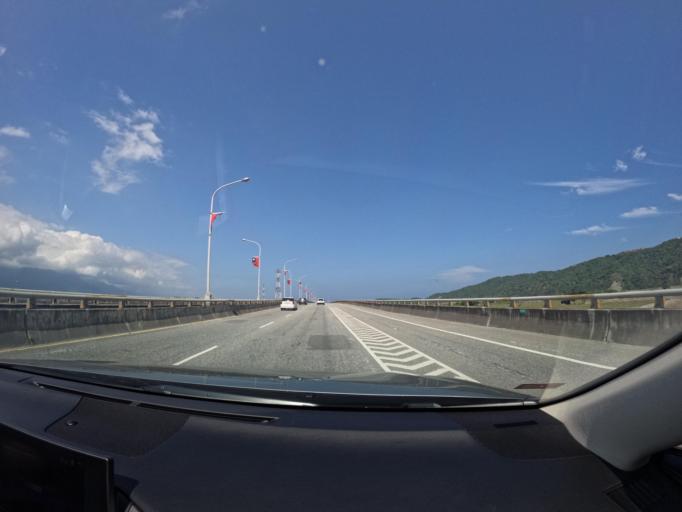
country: TW
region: Taiwan
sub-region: Hualien
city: Hualian
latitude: 23.9112
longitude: 121.5769
